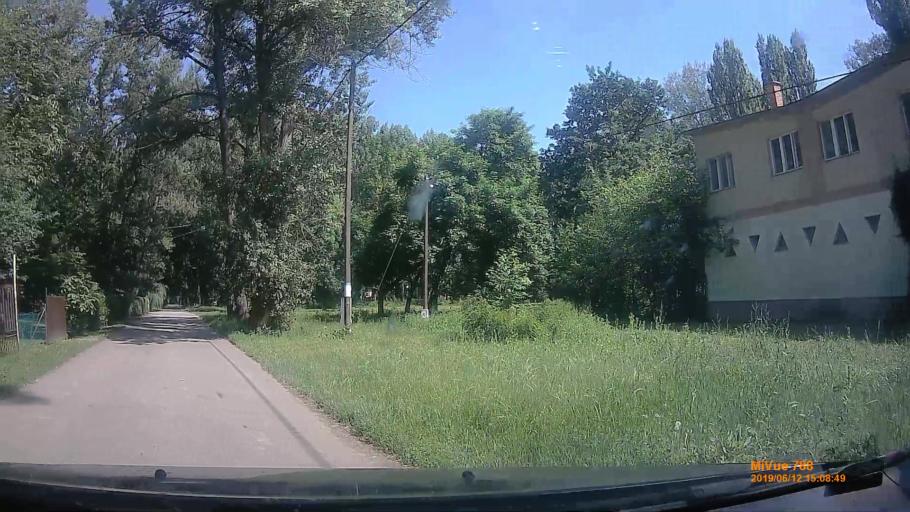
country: HU
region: Csongrad
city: Mako
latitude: 46.1991
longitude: 20.4696
